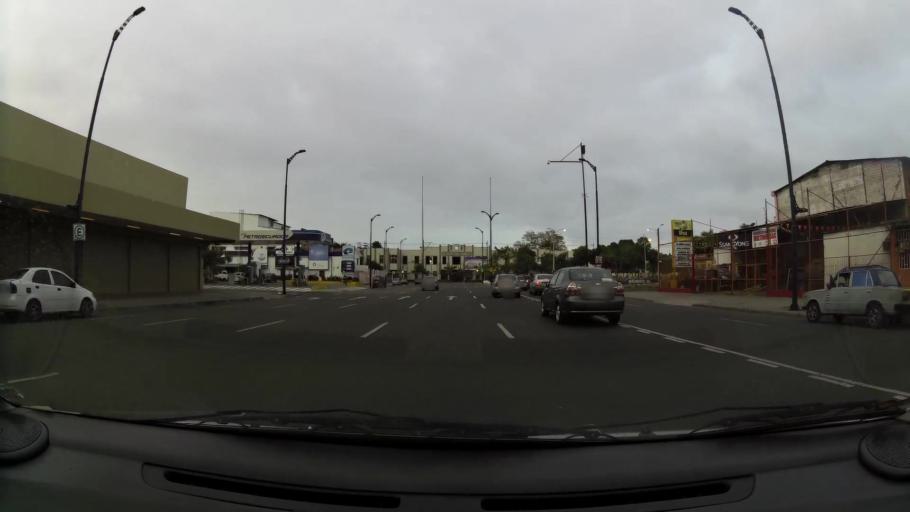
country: EC
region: Guayas
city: Guayaquil
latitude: -2.2012
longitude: -79.8937
